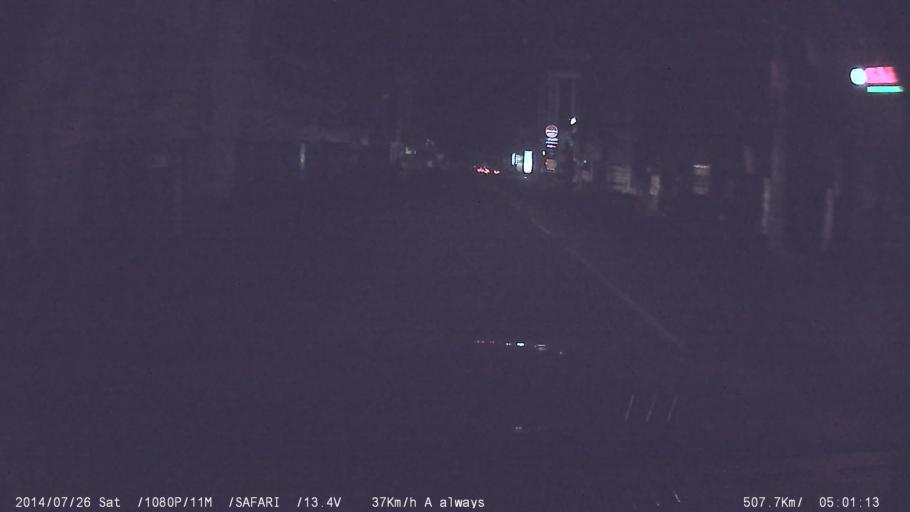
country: IN
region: Kerala
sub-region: Ernakulam
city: Perumpavur
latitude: 10.1142
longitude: 76.4781
